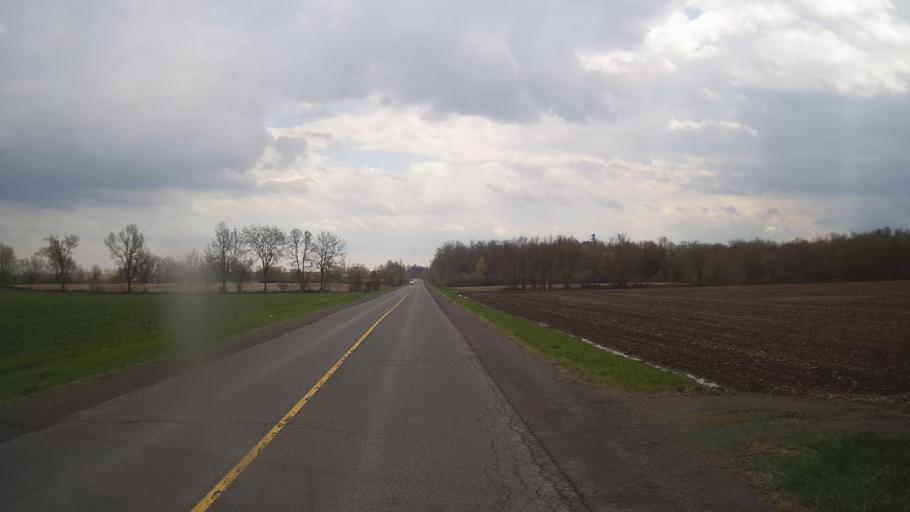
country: CA
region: Ontario
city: Hawkesbury
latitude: 45.5281
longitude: -74.5611
